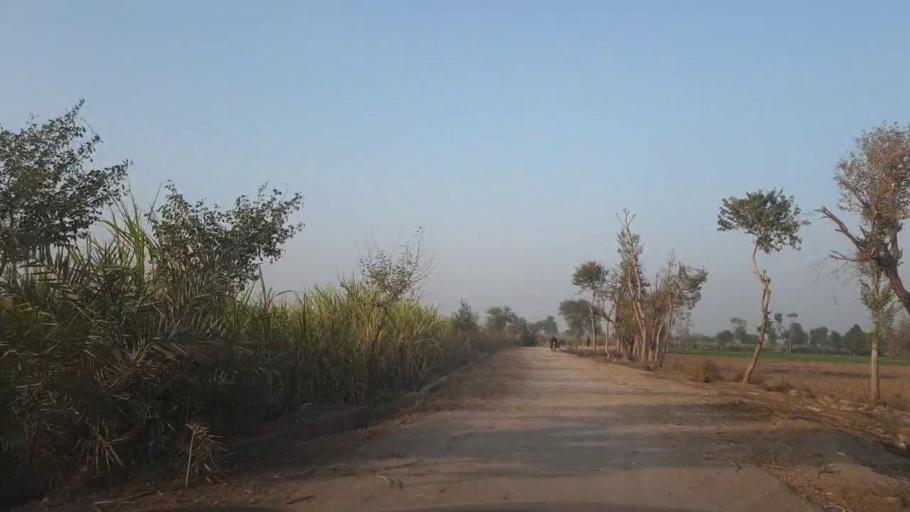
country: PK
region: Sindh
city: Ubauro
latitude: 28.3240
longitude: 69.7762
